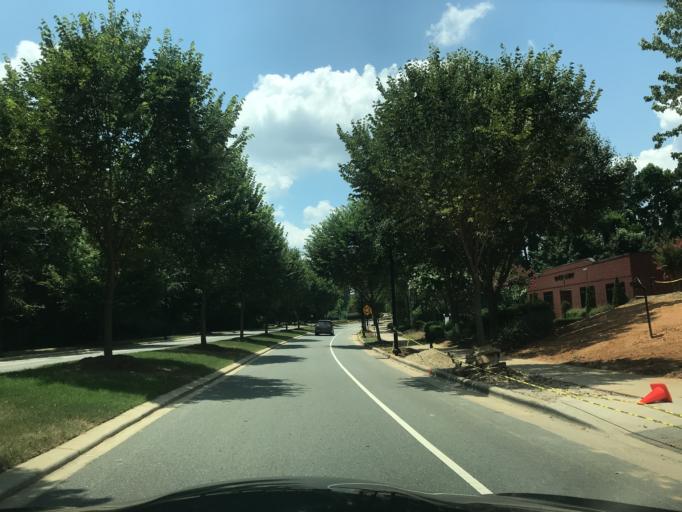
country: US
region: North Carolina
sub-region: Wake County
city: Wake Forest
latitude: 35.9707
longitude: -78.5078
